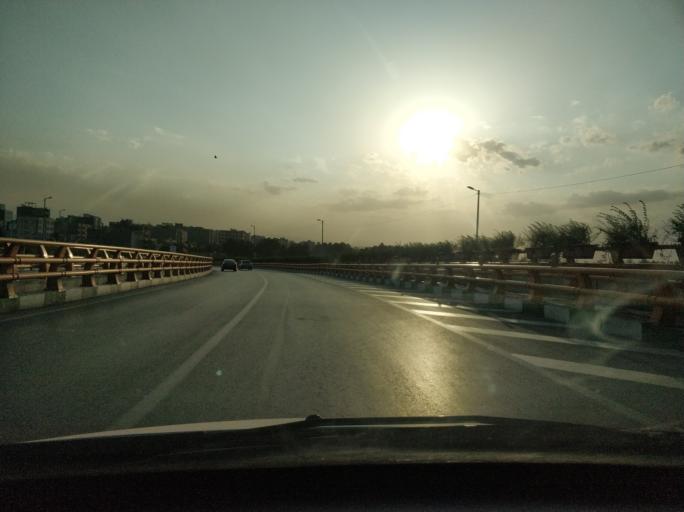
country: IR
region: Razavi Khorasan
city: Mashhad
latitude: 36.3401
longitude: 59.5465
